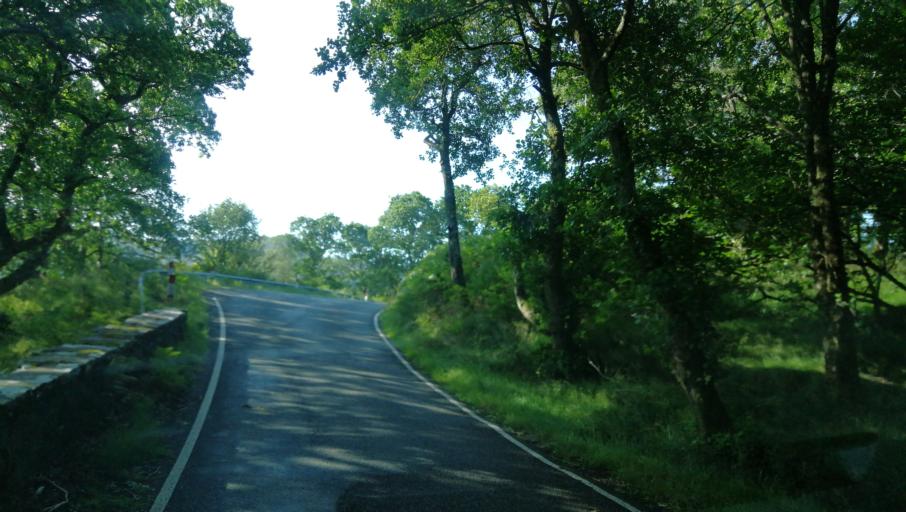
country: GB
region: Scotland
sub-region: Argyll and Bute
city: Isle Of Mull
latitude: 56.6816
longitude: -5.8279
